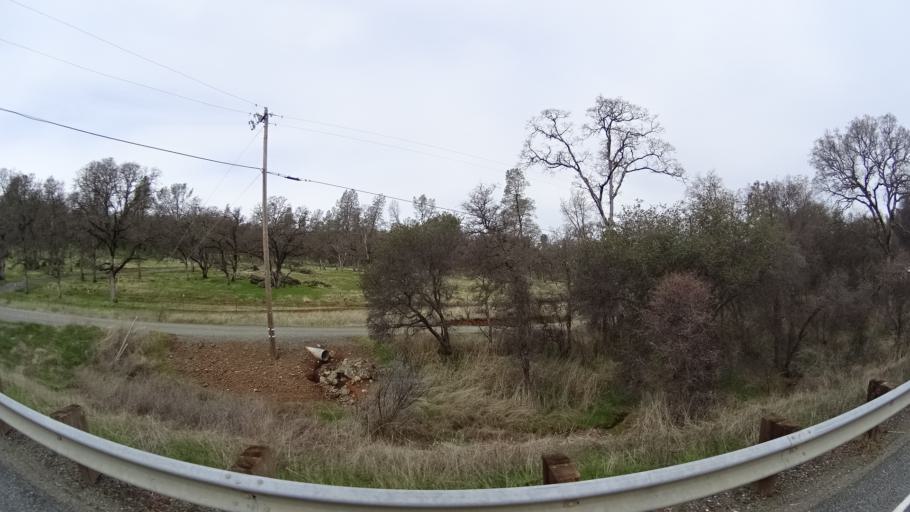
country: US
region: California
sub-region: Yuba County
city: Loma Rica
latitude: 39.3788
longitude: -121.4129
